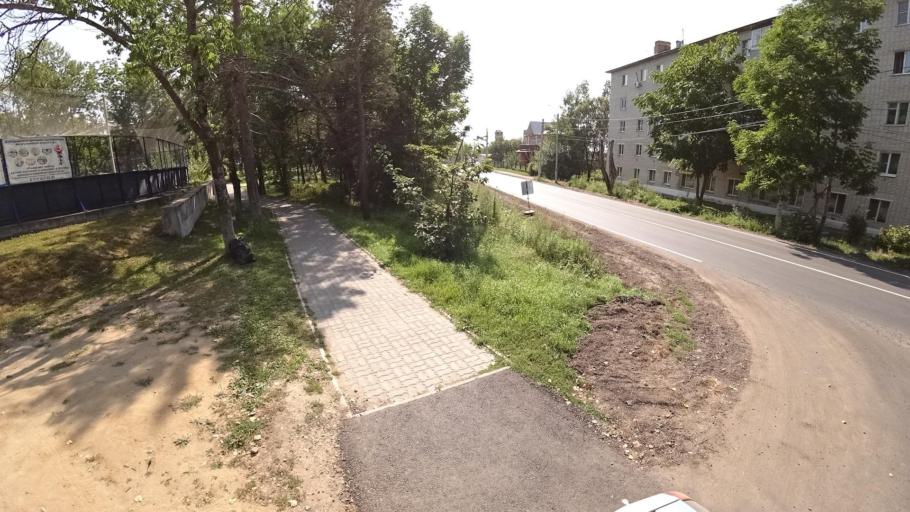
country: RU
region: Khabarovsk Krai
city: Khor
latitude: 47.9642
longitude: 135.0532
